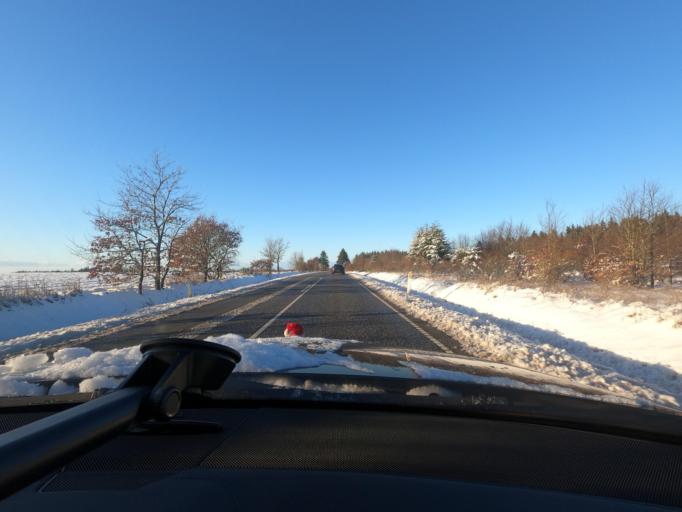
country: DK
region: South Denmark
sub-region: Tonder Kommune
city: Logumkloster
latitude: 55.1712
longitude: 8.9548
